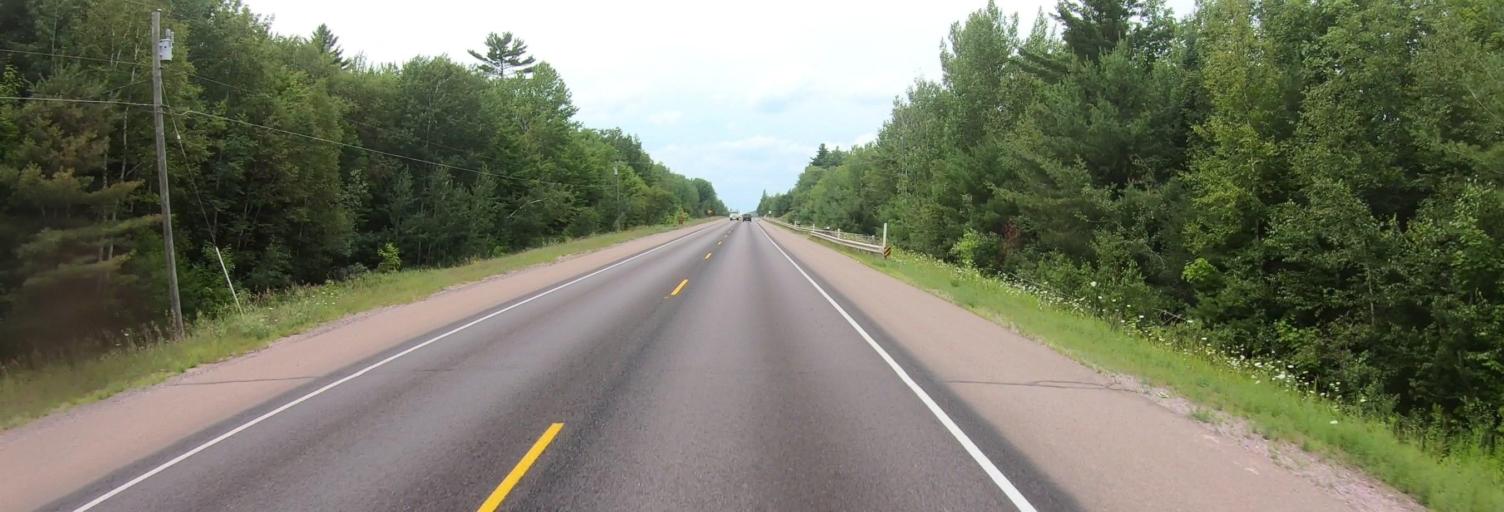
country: US
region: Michigan
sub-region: Marquette County
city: Trowbridge Park
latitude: 46.4723
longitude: -87.4450
